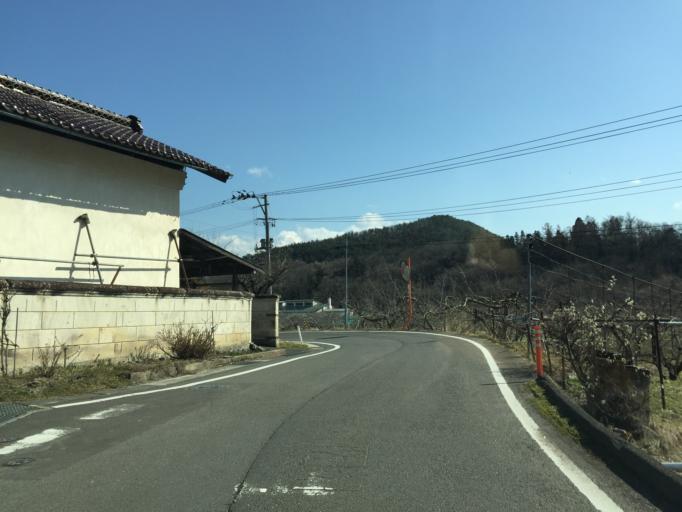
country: JP
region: Fukushima
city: Fukushima-shi
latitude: 37.8235
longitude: 140.4180
